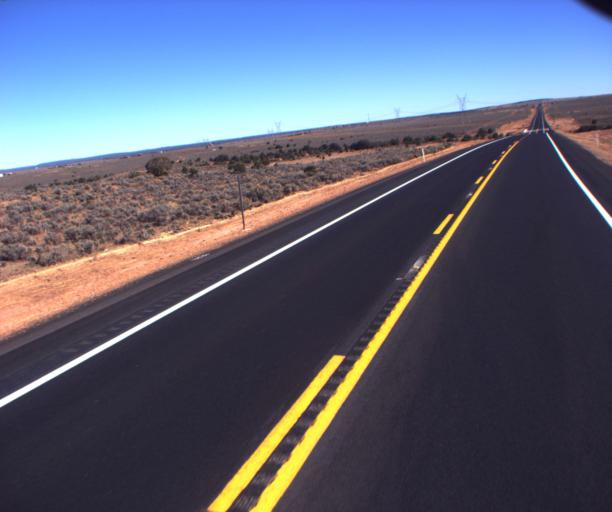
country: US
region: Arizona
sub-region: Apache County
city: Ganado
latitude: 35.7187
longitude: -109.4687
